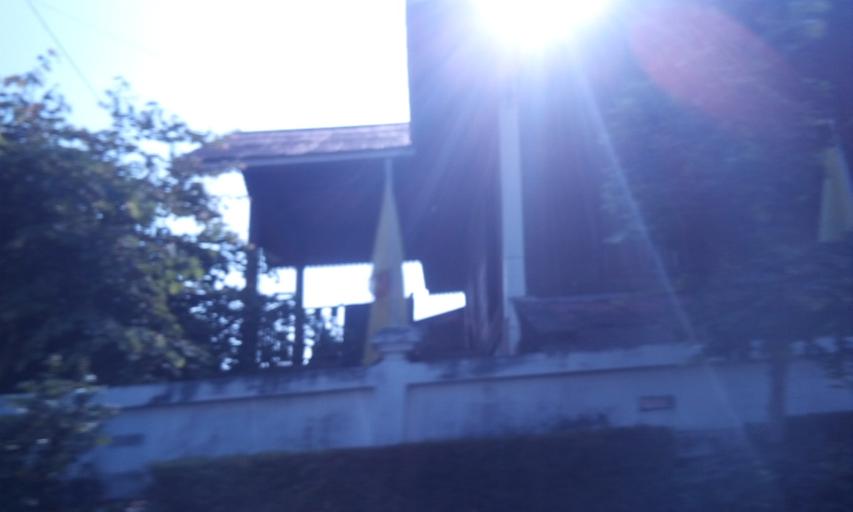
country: TH
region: Pathum Thani
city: Lam Luk Ka
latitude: 13.9516
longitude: 100.7058
